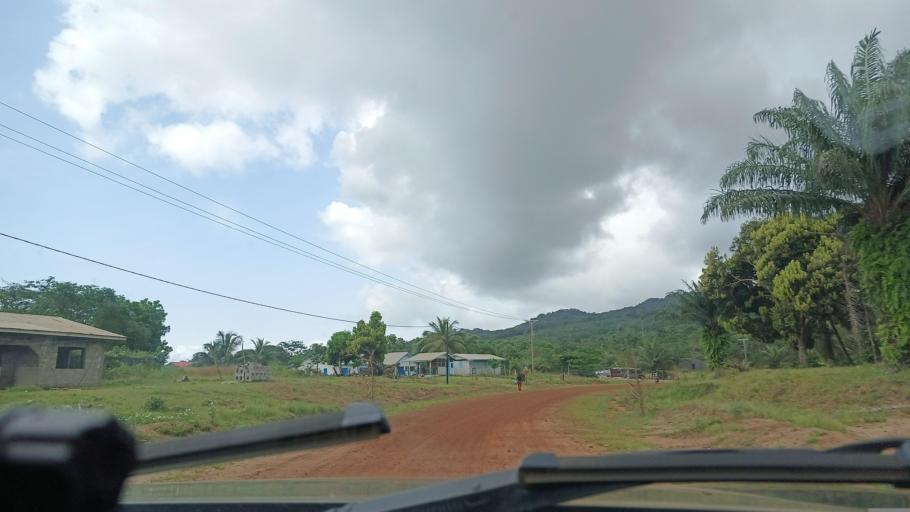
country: LR
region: Grand Cape Mount
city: Robertsport
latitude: 6.7058
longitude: -11.3329
